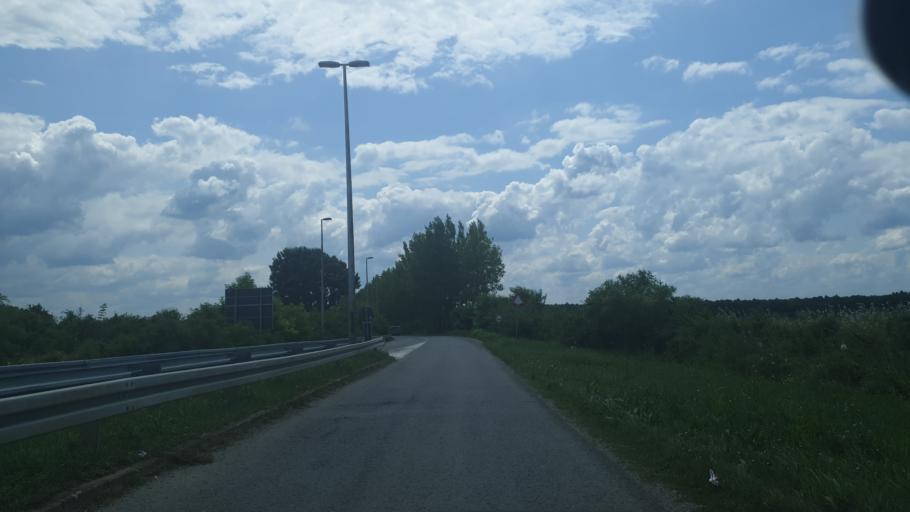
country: RS
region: Autonomna Pokrajina Vojvodina
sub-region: Sremski Okrug
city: Sid
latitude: 45.0450
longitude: 19.2134
